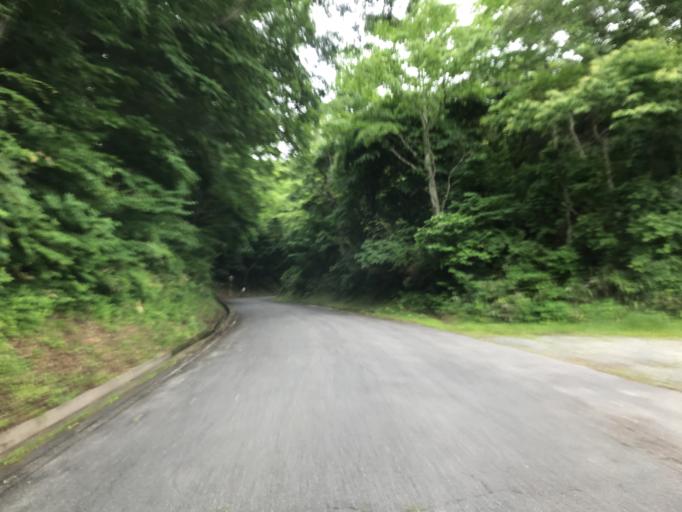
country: JP
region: Fukushima
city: Funehikimachi-funehiki
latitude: 37.4194
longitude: 140.7221
